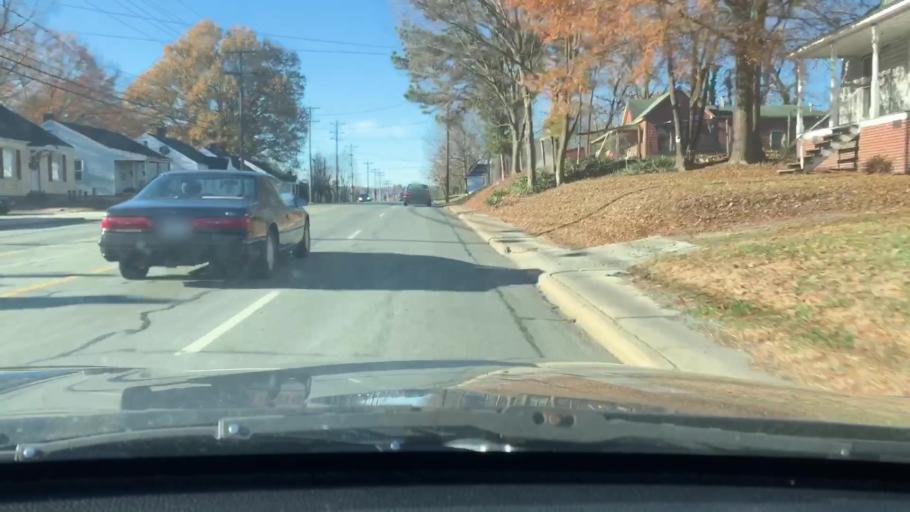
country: US
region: North Carolina
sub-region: Alamance County
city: Burlington
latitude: 36.0864
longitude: -79.4386
